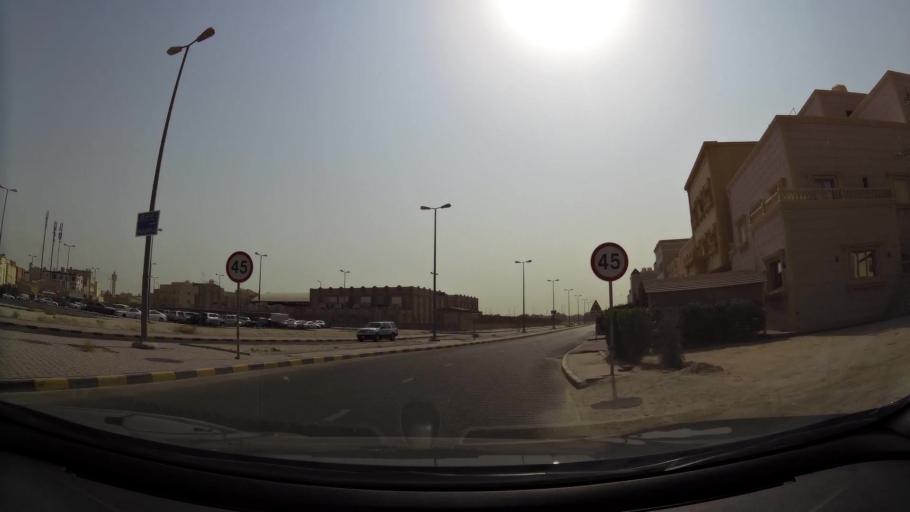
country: KW
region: Muhafazat al Jahra'
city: Al Jahra'
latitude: 29.3387
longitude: 47.7694
